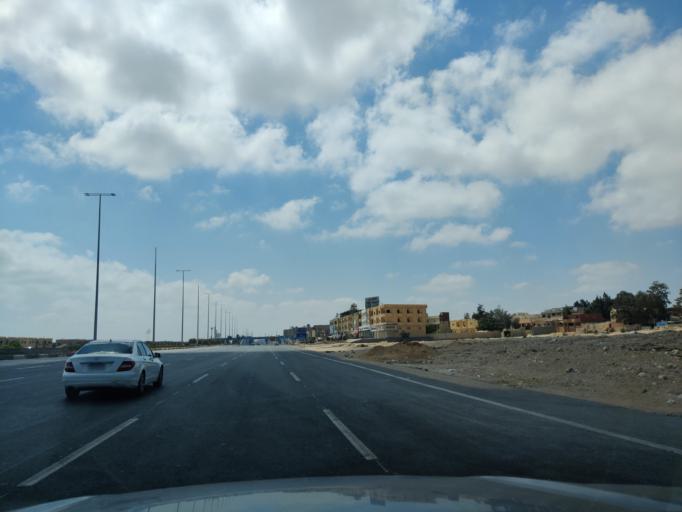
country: EG
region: Muhafazat Matruh
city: Al `Alamayn
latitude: 30.8432
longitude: 28.9458
